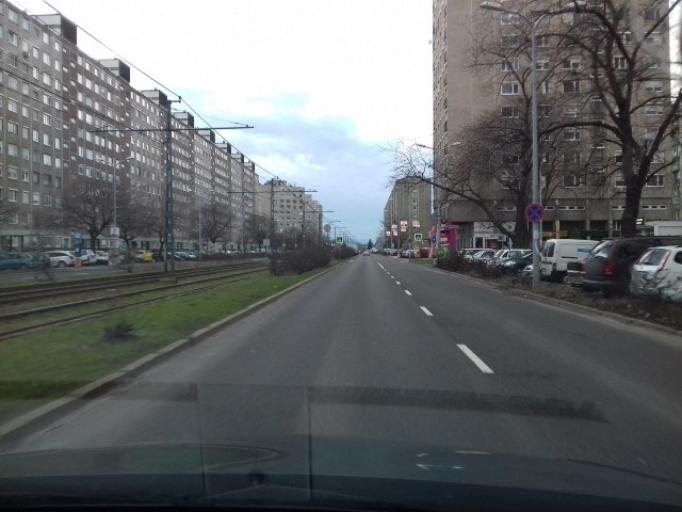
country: HU
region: Budapest
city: Budapest XV. keruelet
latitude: 47.5465
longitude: 19.1366
